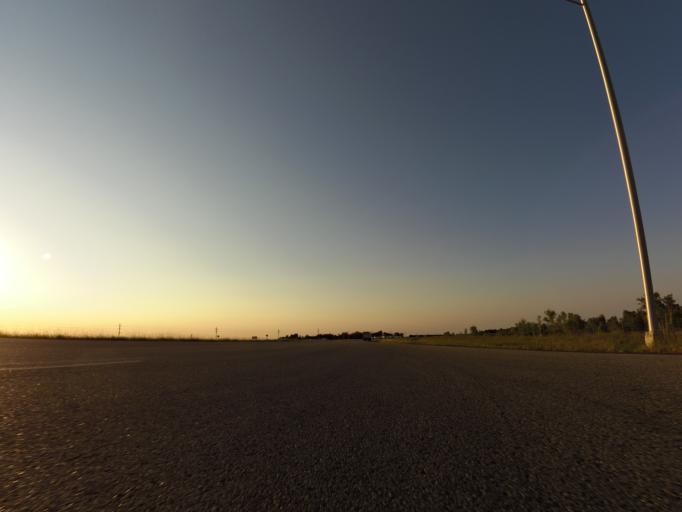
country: US
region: Kansas
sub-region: Reno County
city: South Hutchinson
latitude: 37.9741
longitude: -97.9382
